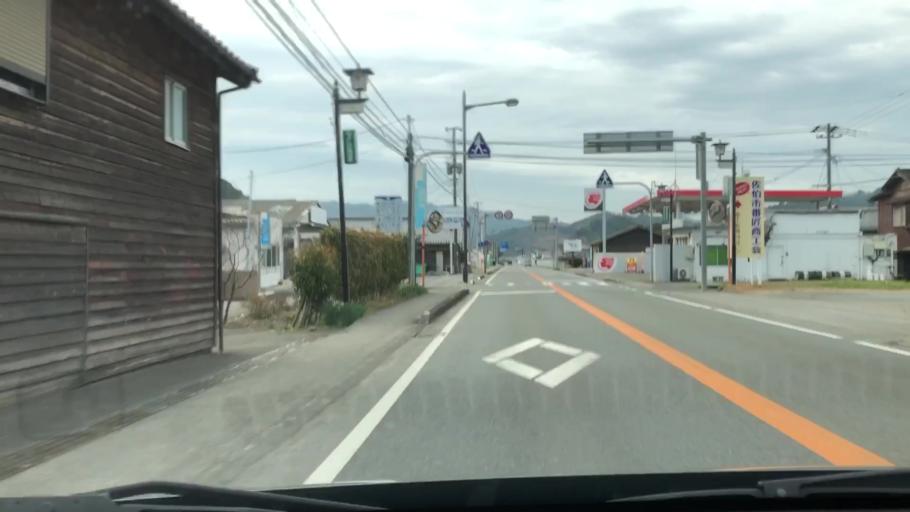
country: JP
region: Oita
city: Saiki
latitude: 32.9681
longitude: 131.8383
